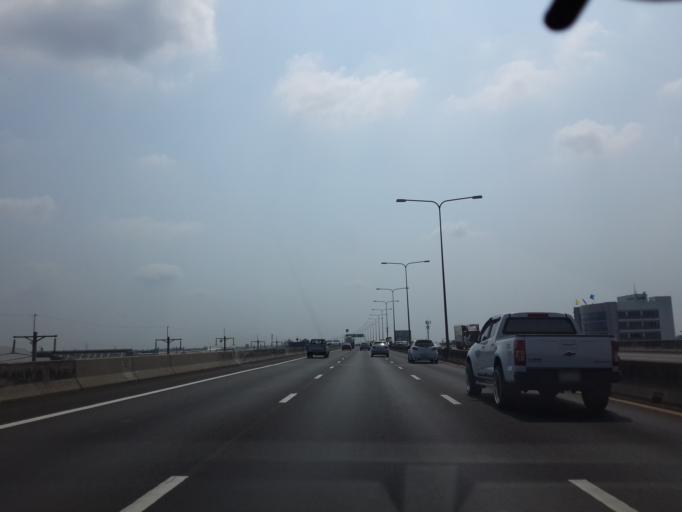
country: TH
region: Samut Prakan
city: Bang Bo District
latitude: 13.6125
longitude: 100.7562
